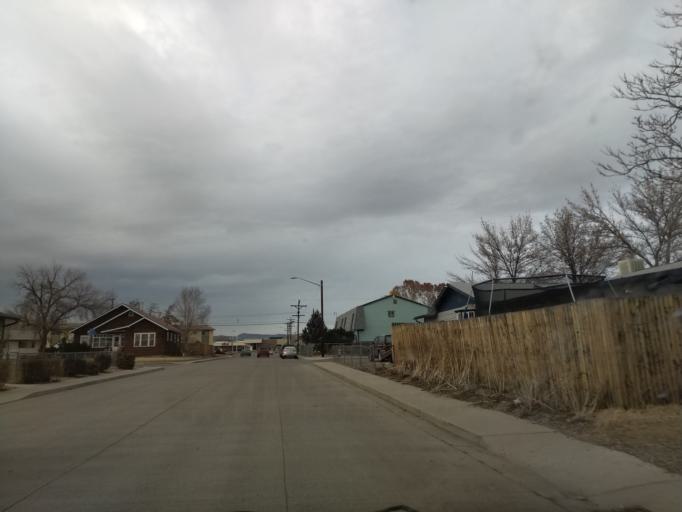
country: US
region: Colorado
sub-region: Mesa County
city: Grand Junction
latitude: 39.0737
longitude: -108.5374
